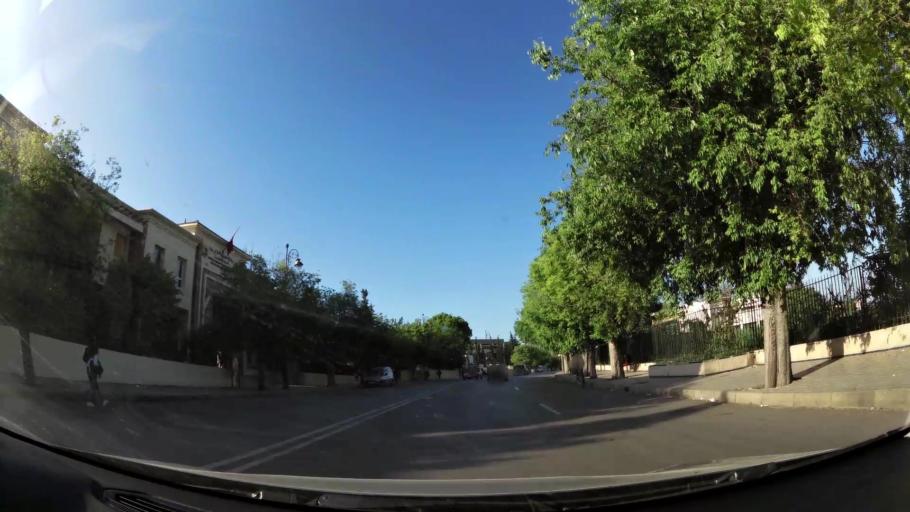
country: MA
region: Fes-Boulemane
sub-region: Fes
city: Fes
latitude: 34.0554
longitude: -4.9853
